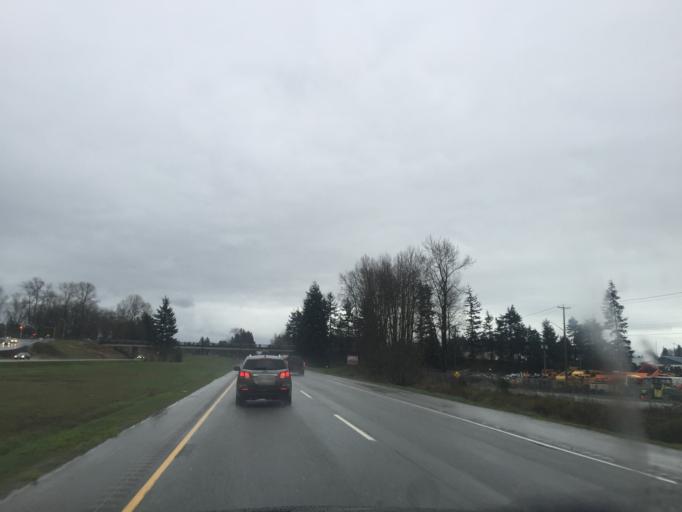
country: US
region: Washington
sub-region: Whatcom County
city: Sumas
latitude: 49.0479
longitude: -122.3586
